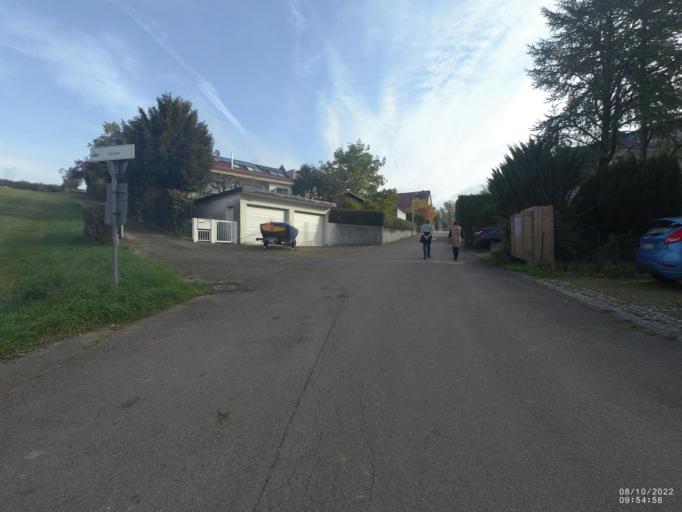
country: DE
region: Baden-Wuerttemberg
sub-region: Regierungsbezirk Stuttgart
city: Wangen
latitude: 48.7221
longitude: 9.6021
